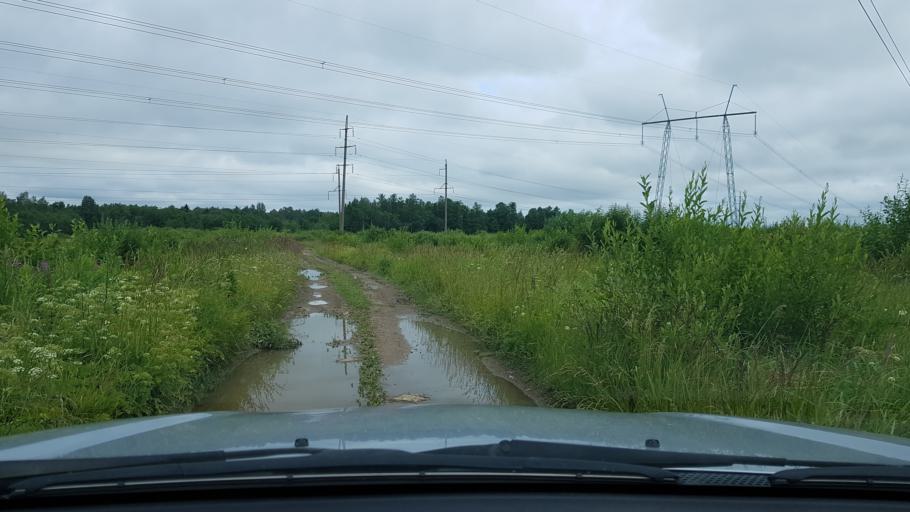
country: EE
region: Ida-Virumaa
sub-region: Narva-Joesuu linn
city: Narva-Joesuu
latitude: 59.3644
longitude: 28.0428
